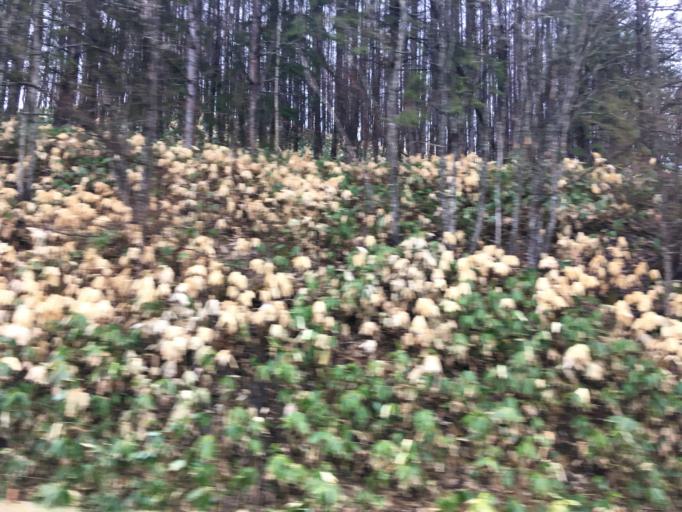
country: JP
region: Hokkaido
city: Nayoro
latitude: 44.0729
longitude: 142.4144
